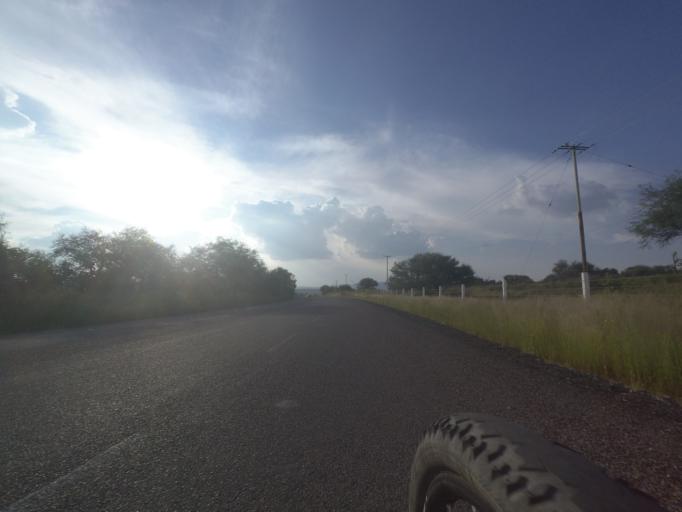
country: MX
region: Aguascalientes
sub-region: Aguascalientes
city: Penuelas (El Cienegal)
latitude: 21.7661
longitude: -102.3547
